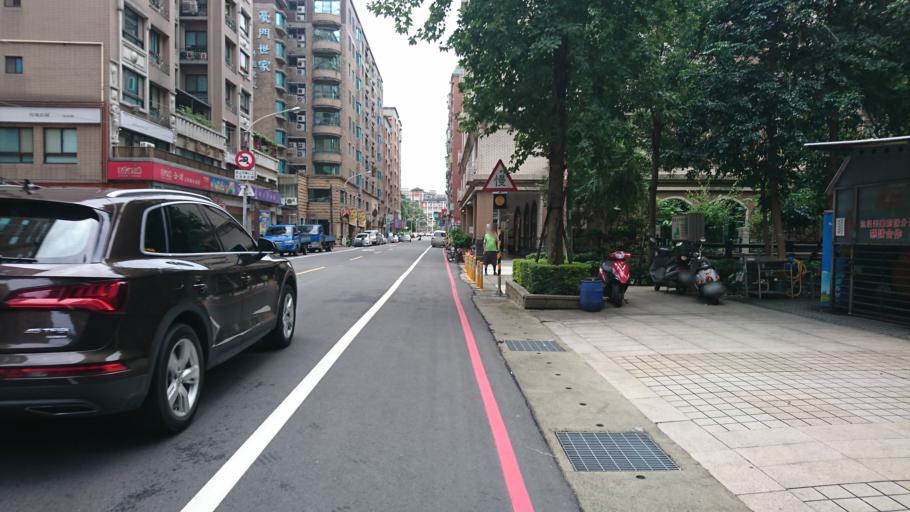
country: TW
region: Taiwan
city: Taoyuan City
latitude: 25.0561
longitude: 121.2968
